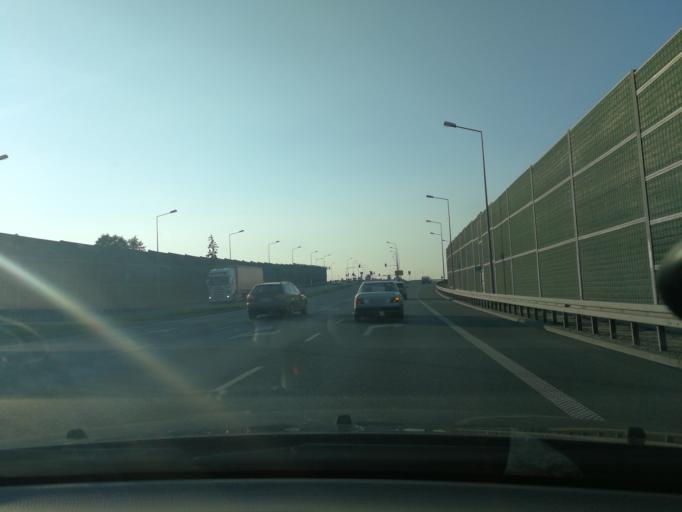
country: PL
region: Masovian Voivodeship
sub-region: Powiat warszawski zachodni
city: Ozarow Mazowiecki
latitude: 52.1847
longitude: 20.7808
